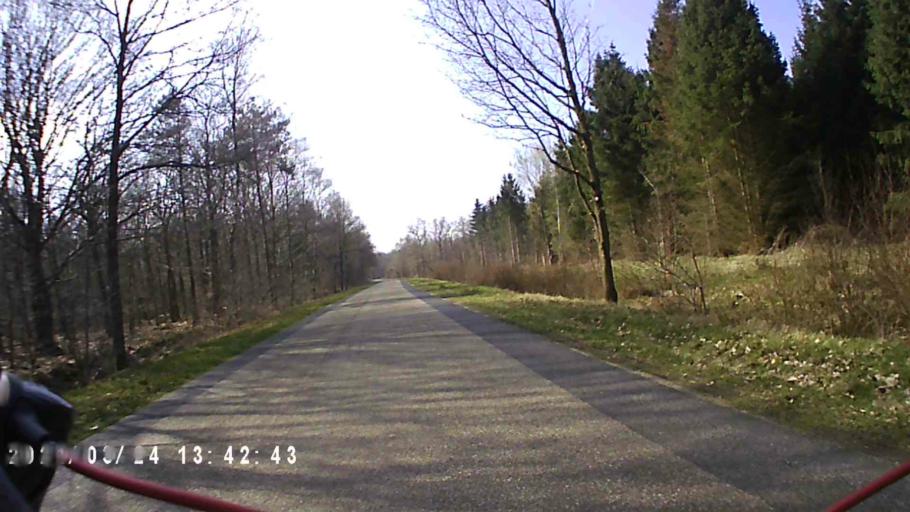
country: NL
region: Groningen
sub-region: Gemeente Grootegast
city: Grootegast
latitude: 53.0872
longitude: 6.2743
